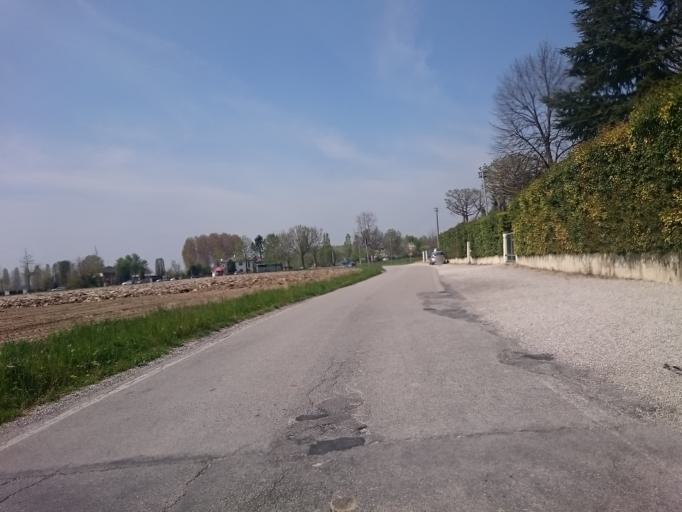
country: IT
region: Veneto
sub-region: Provincia di Padova
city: Rubano
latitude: 45.4338
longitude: 11.7925
